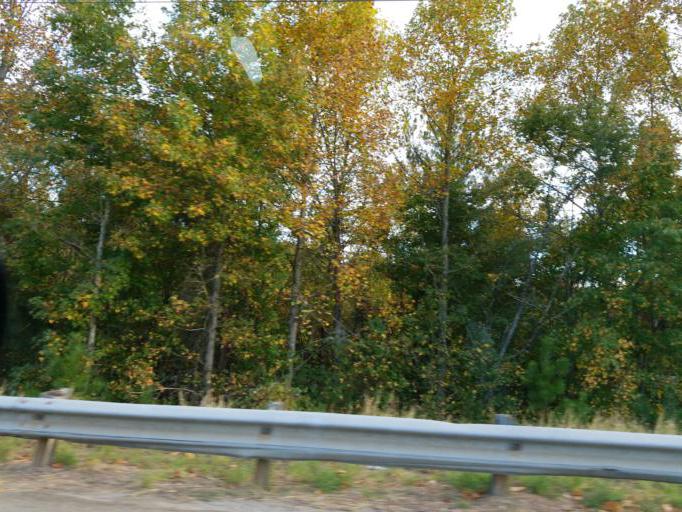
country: US
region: Georgia
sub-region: Bartow County
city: Cartersville
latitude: 34.1735
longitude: -84.7613
